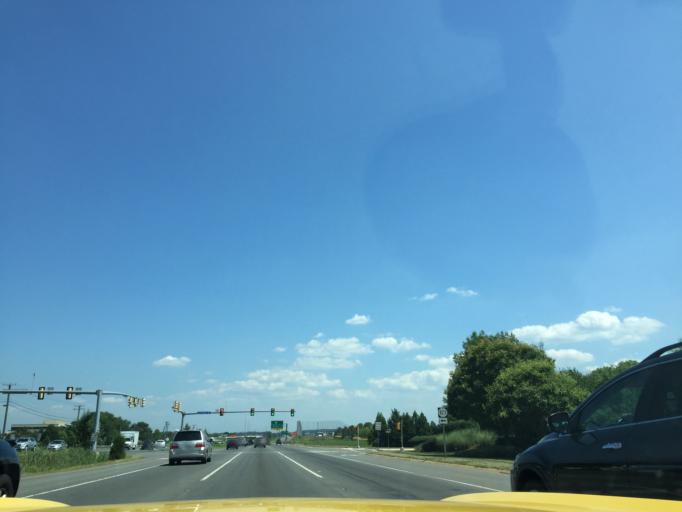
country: US
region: Virginia
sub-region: Loudoun County
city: University Center
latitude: 39.0609
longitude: -77.4602
